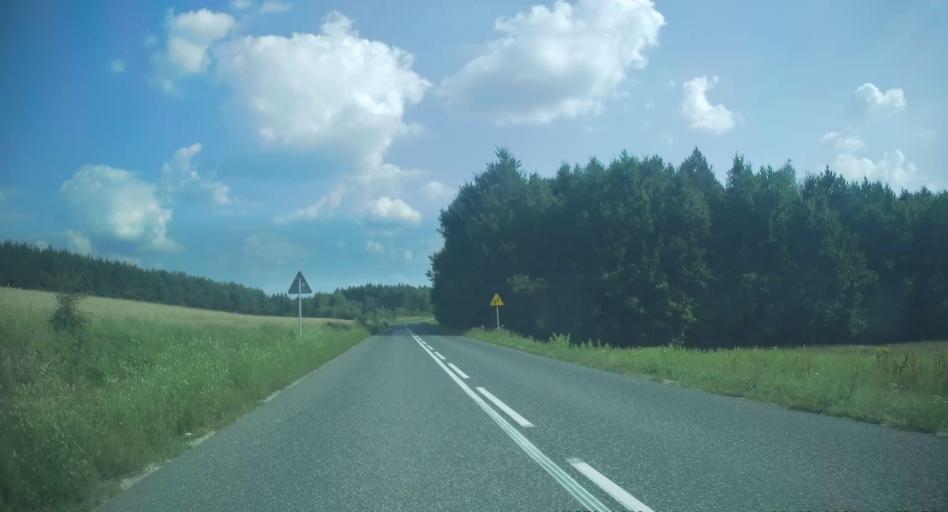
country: PL
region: Swietokrzyskie
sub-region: Powiat kielecki
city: Lopuszno
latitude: 50.8937
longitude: 20.2542
